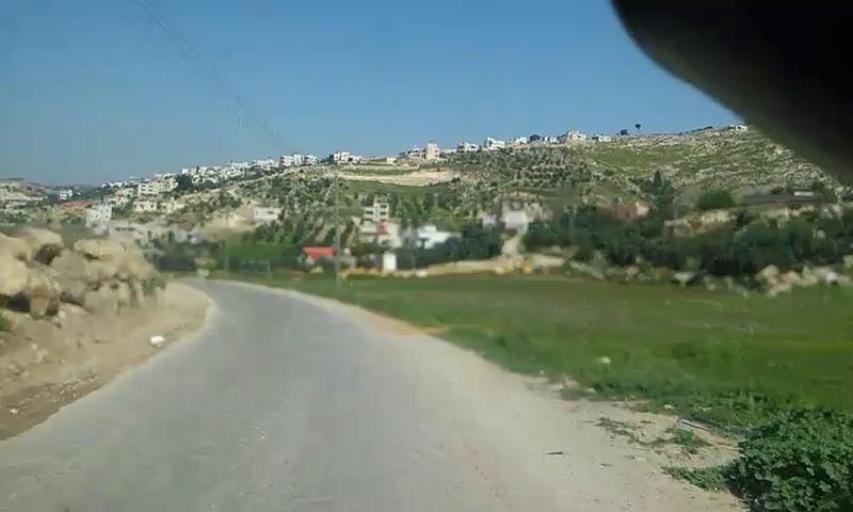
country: PS
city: Dayr Samit
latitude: 31.5065
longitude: 34.9695
